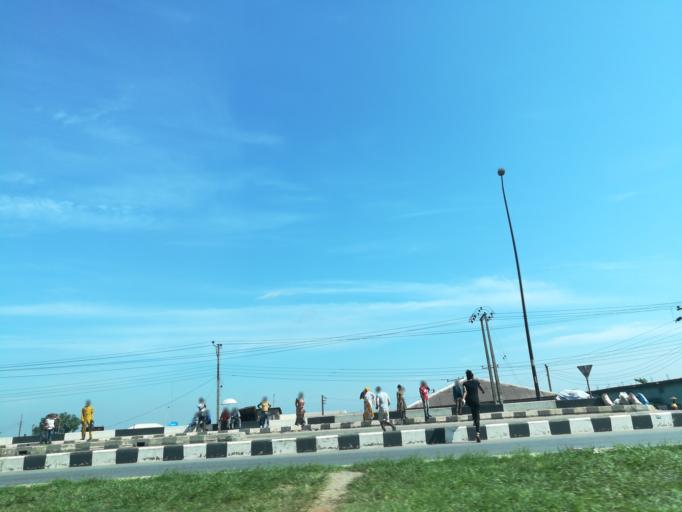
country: NG
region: Lagos
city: Ebute Ikorodu
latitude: 6.6195
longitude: 3.4704
